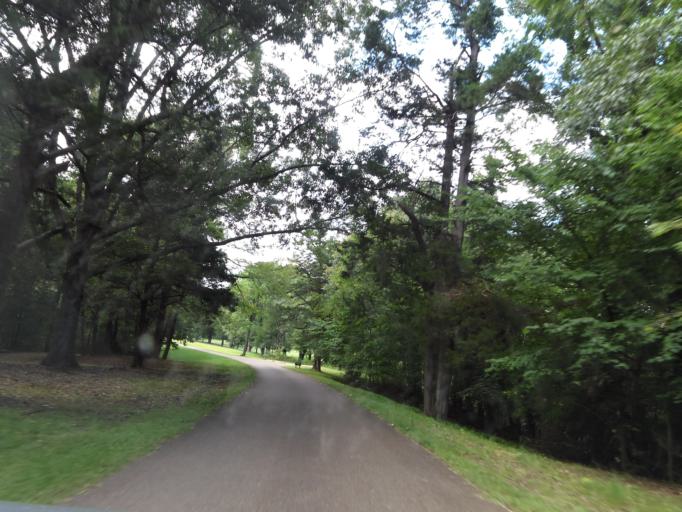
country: US
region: Tennessee
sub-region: Hardin County
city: Crump
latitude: 35.1485
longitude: -88.3196
